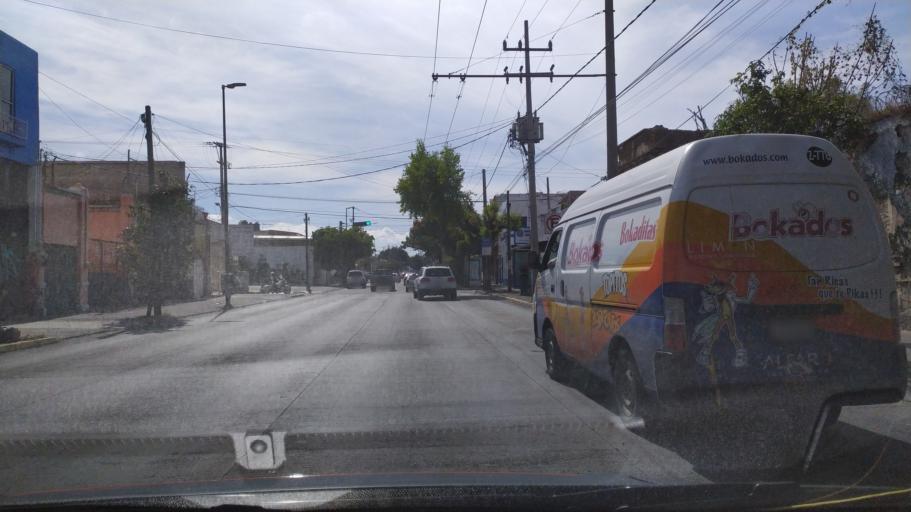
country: MX
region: Jalisco
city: Tlaquepaque
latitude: 20.6760
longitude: -103.3293
